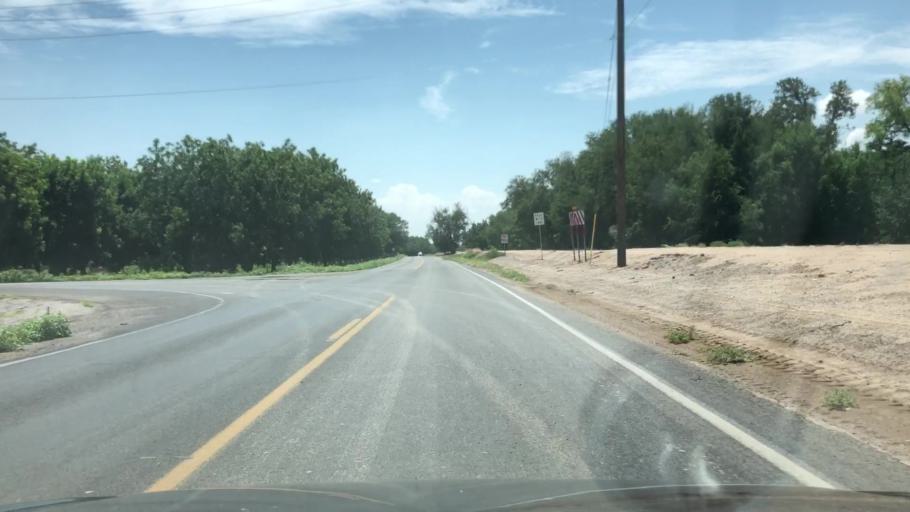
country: US
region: New Mexico
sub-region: Dona Ana County
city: Anthony
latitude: 32.0178
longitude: -106.6686
